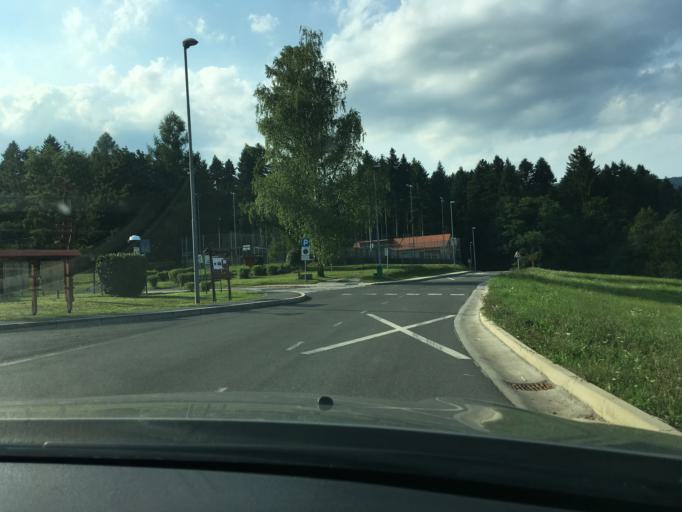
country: SI
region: Dolenjske Toplice
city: Dolenjske Toplice
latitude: 45.7573
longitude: 15.0544
